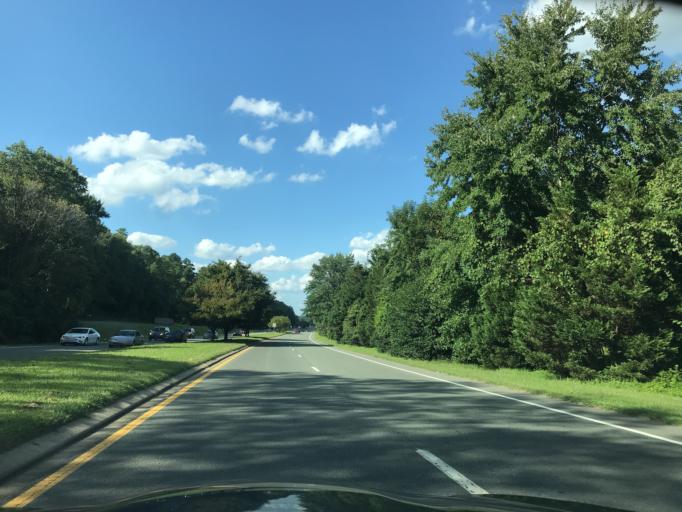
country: US
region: North Carolina
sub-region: Orange County
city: Chapel Hill
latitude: 35.9173
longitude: -79.0262
